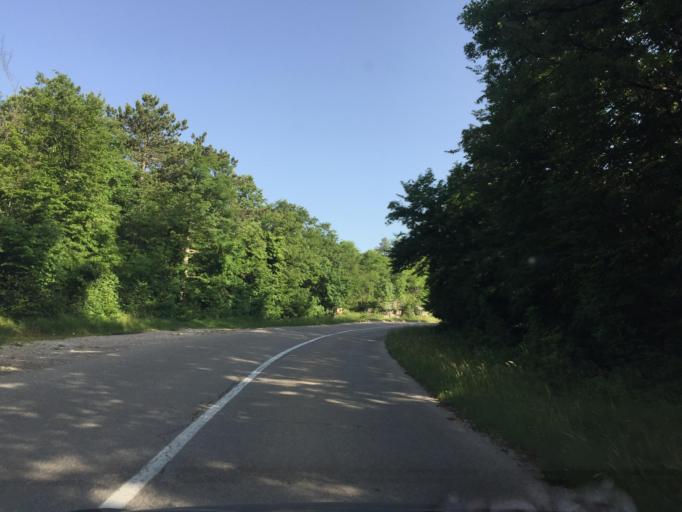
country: HR
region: Primorsko-Goranska
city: Klana
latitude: 45.4324
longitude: 14.3672
